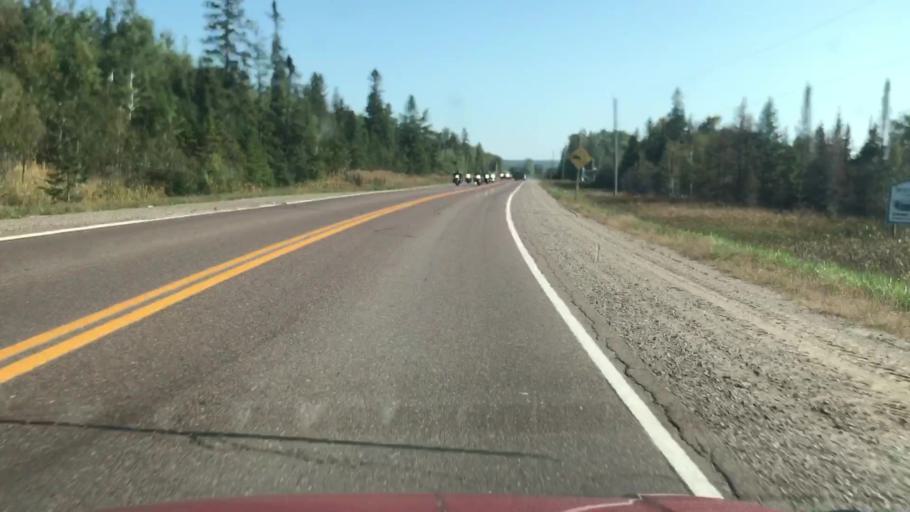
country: CA
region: Ontario
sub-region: Algoma
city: Sault Ste. Marie
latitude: 46.3341
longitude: -84.0054
